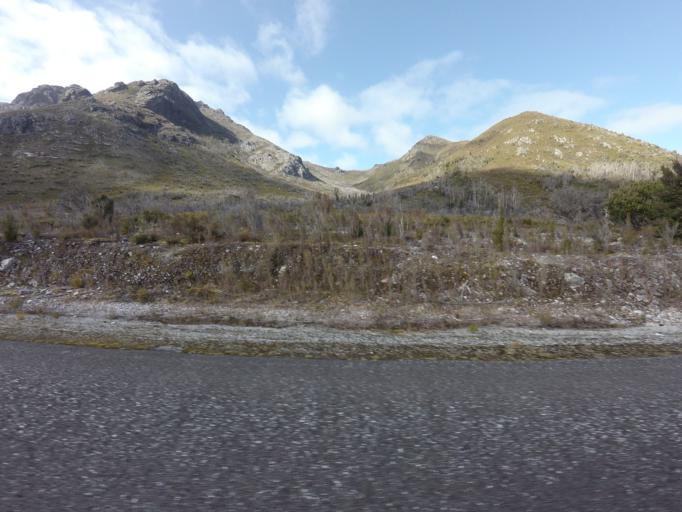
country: AU
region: Tasmania
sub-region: Huon Valley
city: Geeveston
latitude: -42.8612
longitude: 146.2167
